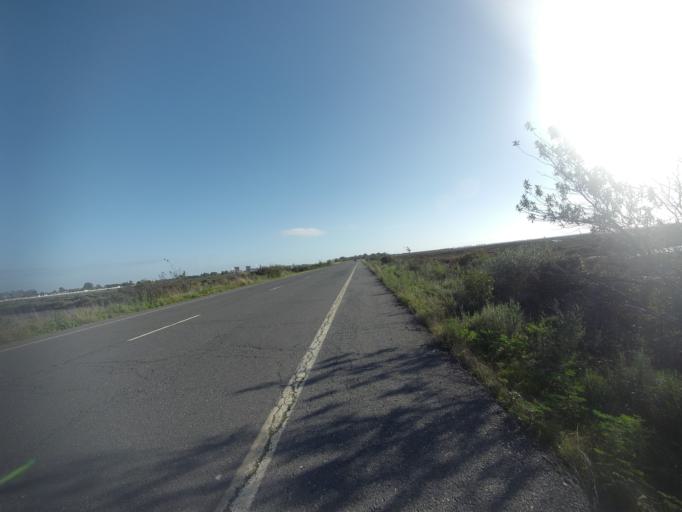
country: ES
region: Andalusia
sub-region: Provincia de Huelva
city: Huelva
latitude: 37.2478
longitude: -6.9671
